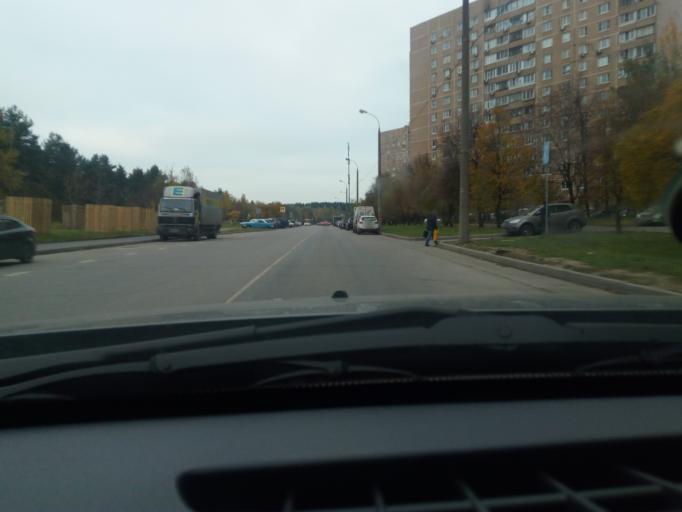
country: RU
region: Moskovskaya
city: Reutov
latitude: 55.7423
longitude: 37.8788
